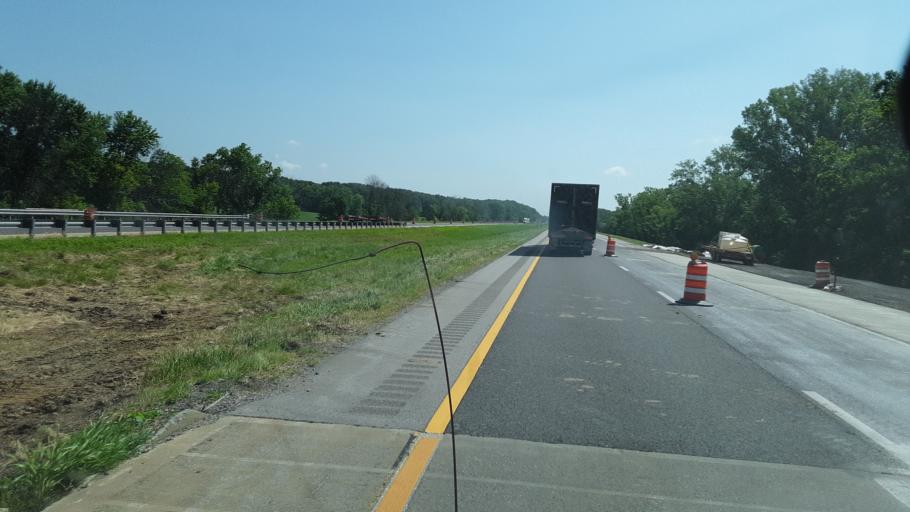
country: US
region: Illinois
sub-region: Cumberland County
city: Toledo
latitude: 39.2029
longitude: -88.2906
